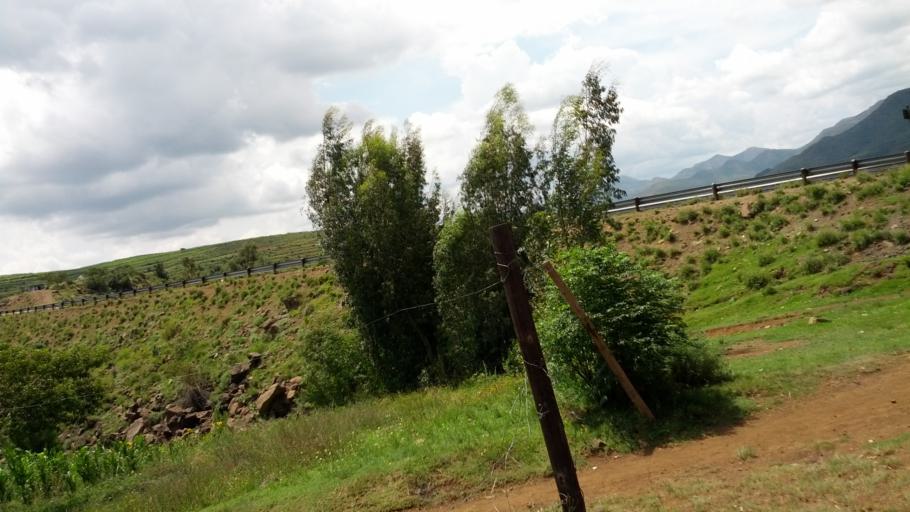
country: LS
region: Maseru
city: Nako
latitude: -29.5923
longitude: 27.7512
